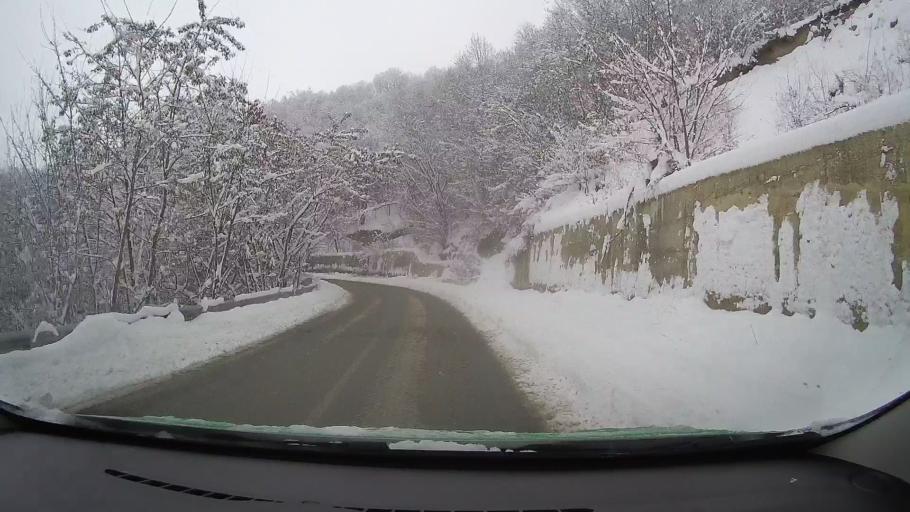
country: RO
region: Sibiu
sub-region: Comuna Jina
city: Jina
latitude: 45.7700
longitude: 23.6694
